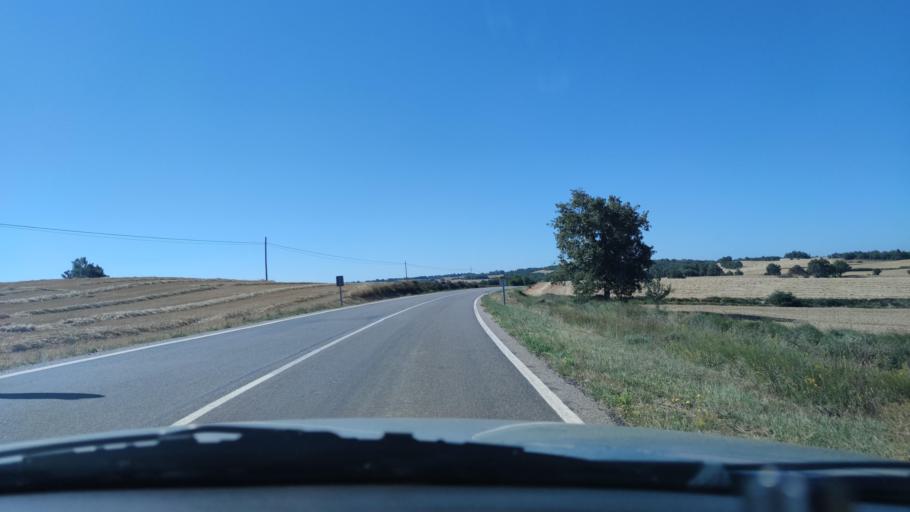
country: ES
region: Catalonia
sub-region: Provincia de Lleida
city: Solsona
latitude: 41.9385
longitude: 1.4970
